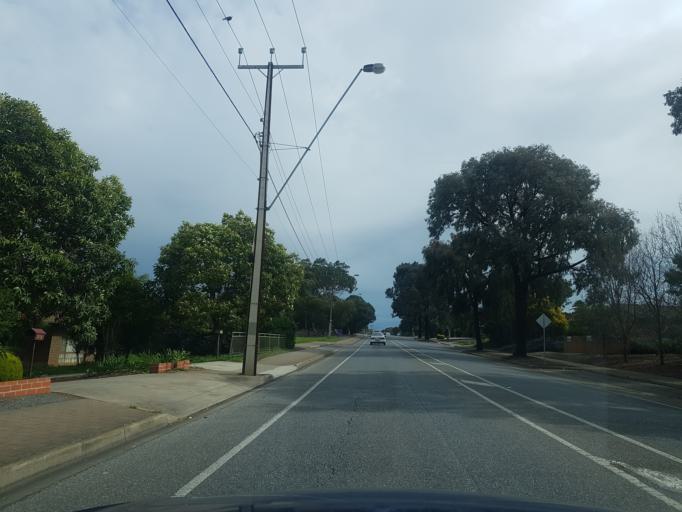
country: AU
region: South Australia
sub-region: Tea Tree Gully
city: Modbury
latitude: -34.8180
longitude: 138.6831
